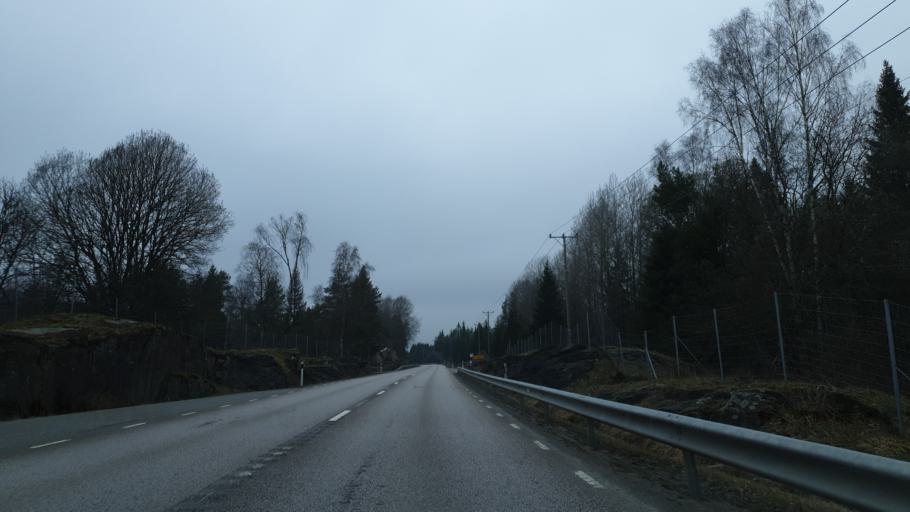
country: SE
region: Vaestra Goetaland
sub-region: Harryda Kommun
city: Hindas
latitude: 57.6342
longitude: 12.4098
